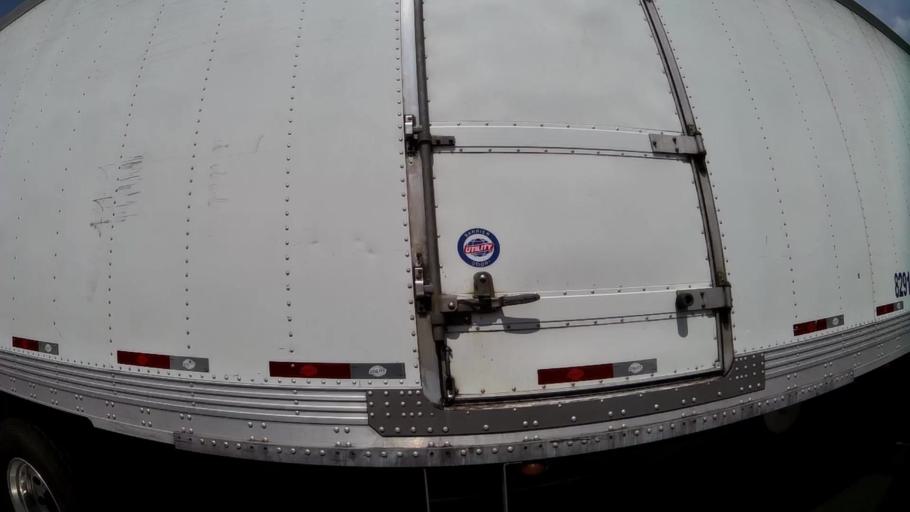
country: PA
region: Panama
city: San Miguelito
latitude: 9.0357
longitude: -79.4836
